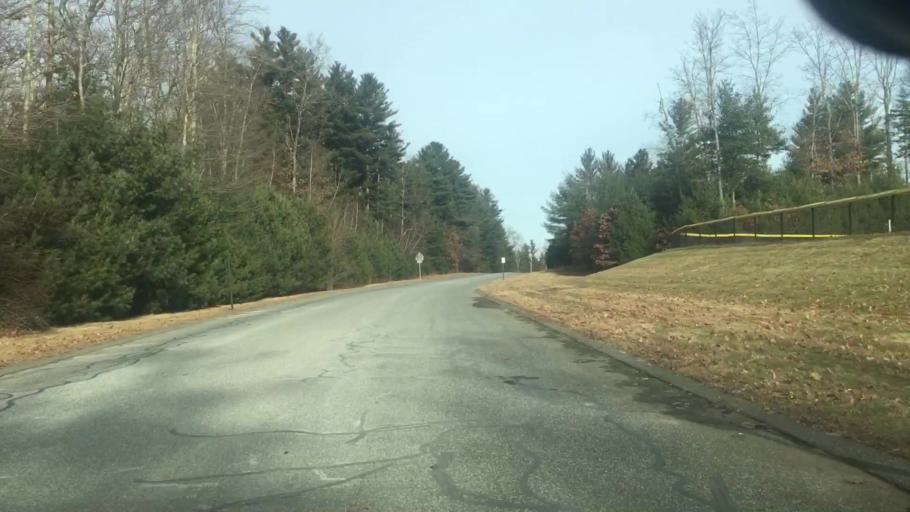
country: US
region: Connecticut
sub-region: Tolland County
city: Stafford Springs
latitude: 41.9731
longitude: -72.3041
